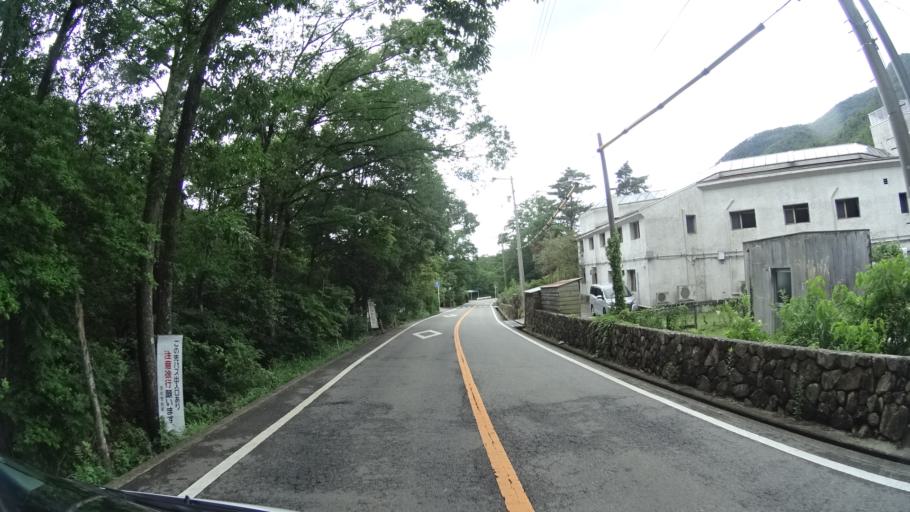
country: JP
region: Kyoto
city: Kameoka
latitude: 35.0059
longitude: 135.4335
